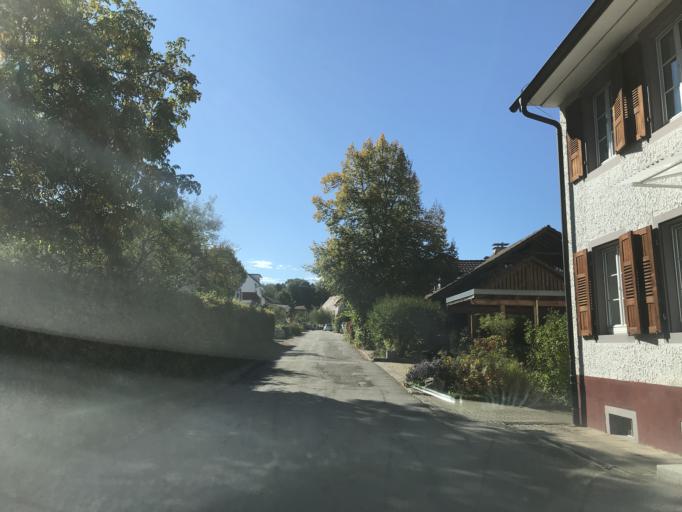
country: DE
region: Baden-Wuerttemberg
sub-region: Freiburg Region
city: Schopfheim
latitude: 47.6381
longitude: 7.8136
